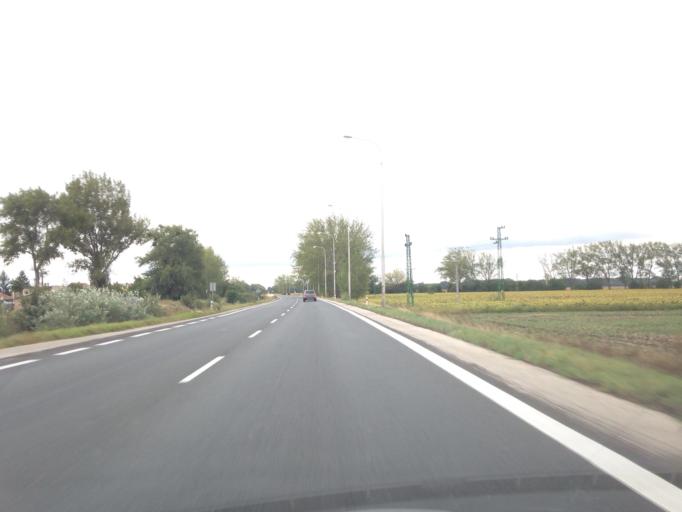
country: SK
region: Nitriansky
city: Komarno
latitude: 47.7875
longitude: 18.1680
